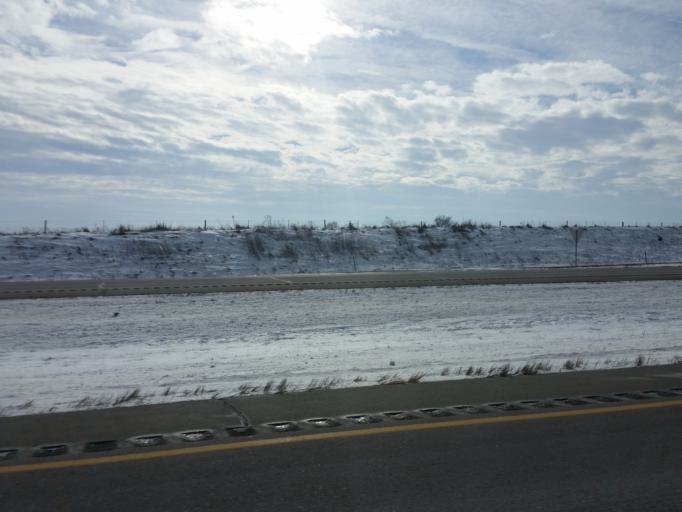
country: US
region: Iowa
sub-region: Buchanan County
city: Independence
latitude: 42.4618
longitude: -91.7489
